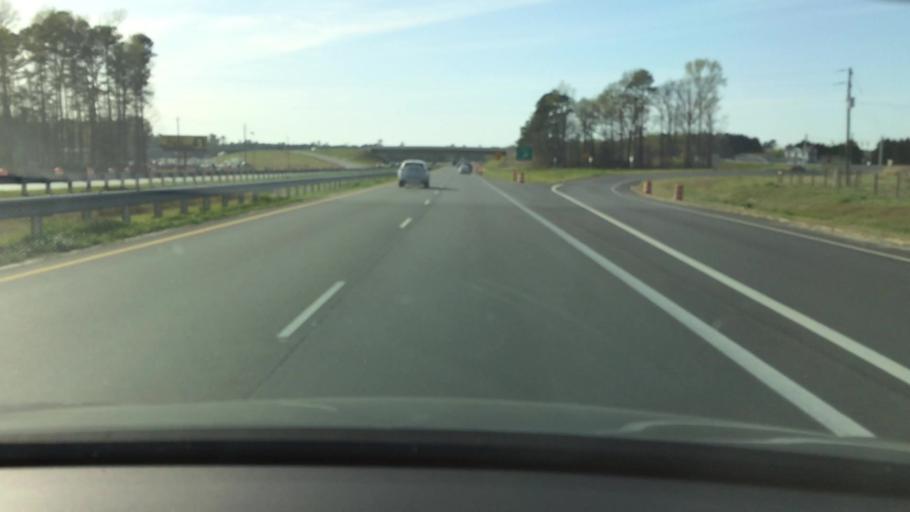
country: US
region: North Carolina
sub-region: Johnston County
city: Pine Level
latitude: 35.4899
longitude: -78.2665
